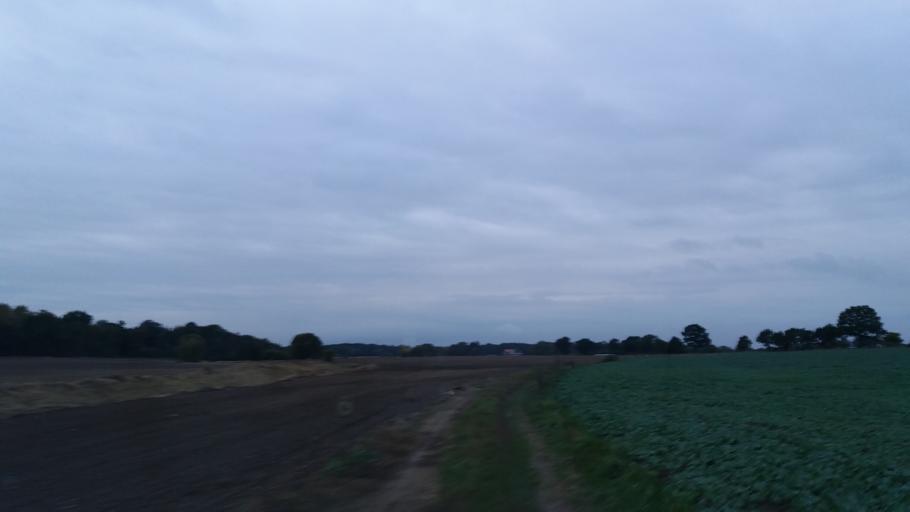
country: PL
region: West Pomeranian Voivodeship
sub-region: Powiat choszczenski
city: Krzecin
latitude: 53.0854
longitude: 15.4087
